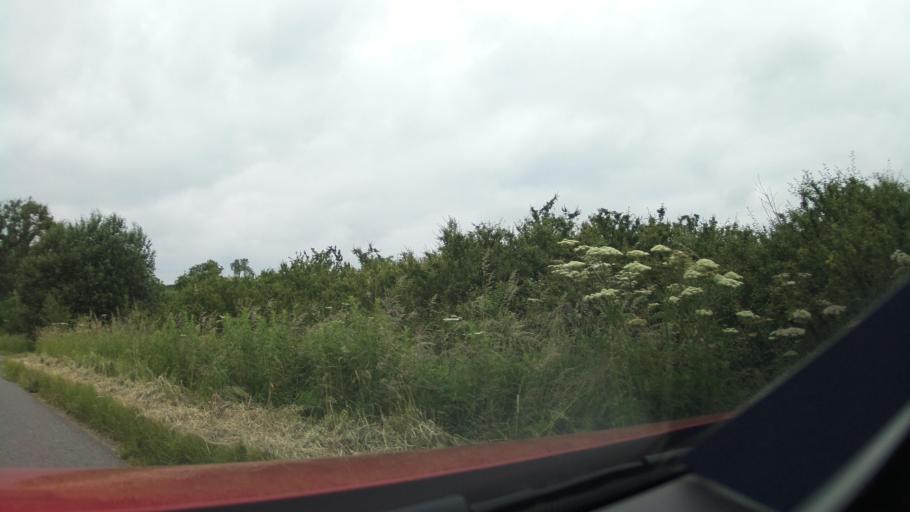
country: GB
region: England
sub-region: District of Rutland
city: Langham
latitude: 52.6756
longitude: -0.7921
